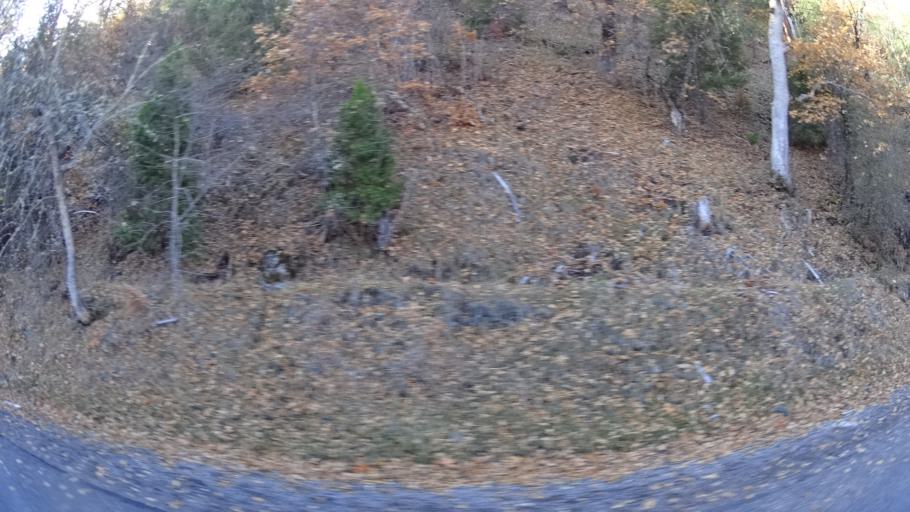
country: US
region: California
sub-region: Siskiyou County
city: Yreka
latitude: 41.8319
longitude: -122.8503
